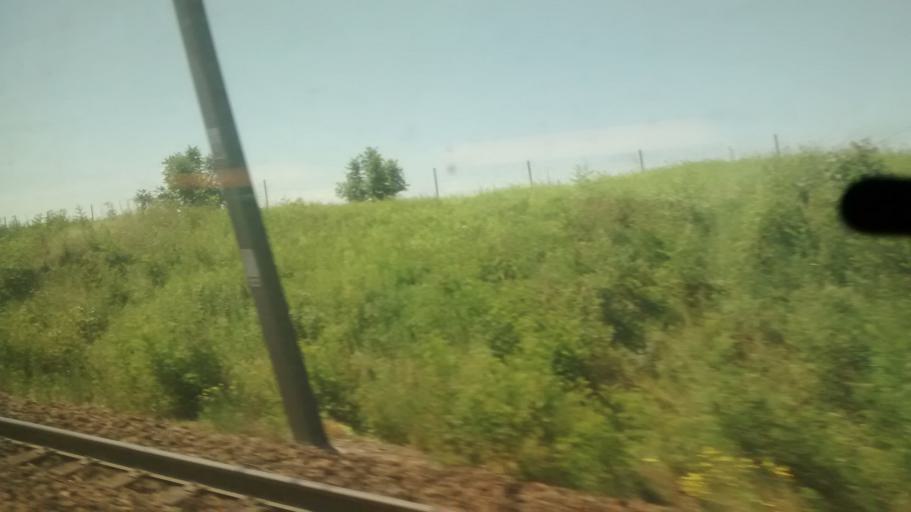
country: FR
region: Rhone-Alpes
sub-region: Departement du Rhone
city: Cailloux-sur-Fontaines
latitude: 45.8556
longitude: 4.8870
